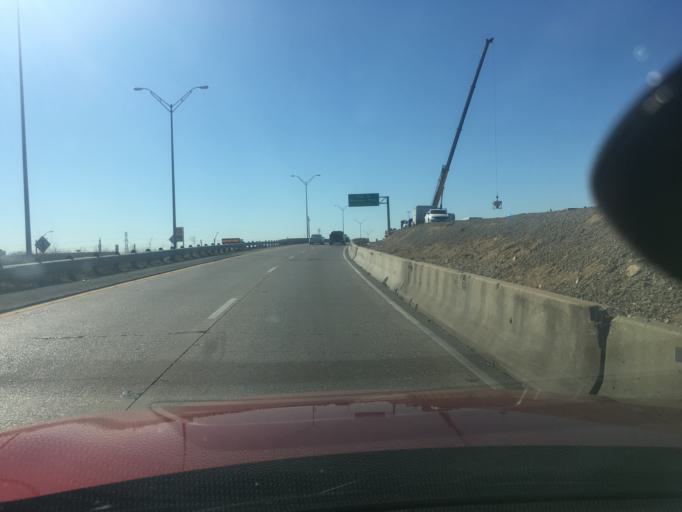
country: US
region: Texas
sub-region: Dallas County
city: Cockrell Hill
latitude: 32.7064
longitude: -96.8311
